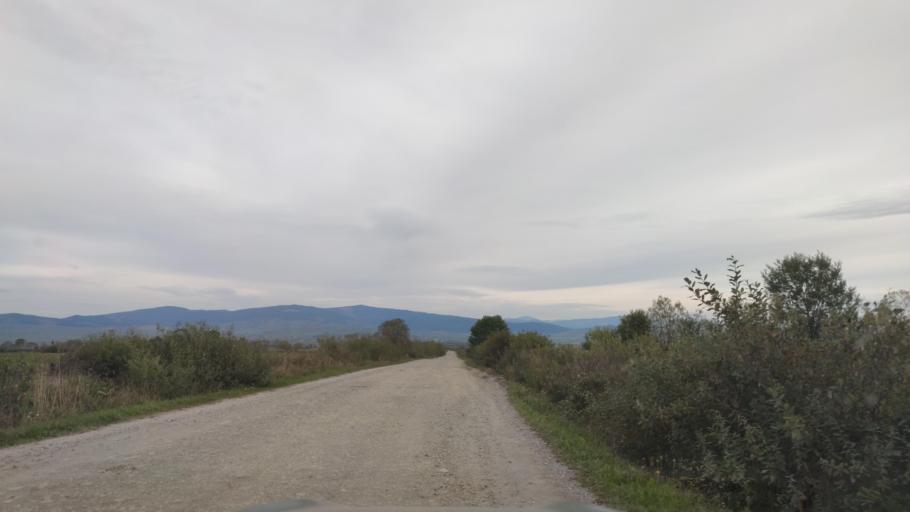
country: RO
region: Harghita
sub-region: Comuna Remetea
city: Remetea
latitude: 46.8098
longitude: 25.3974
